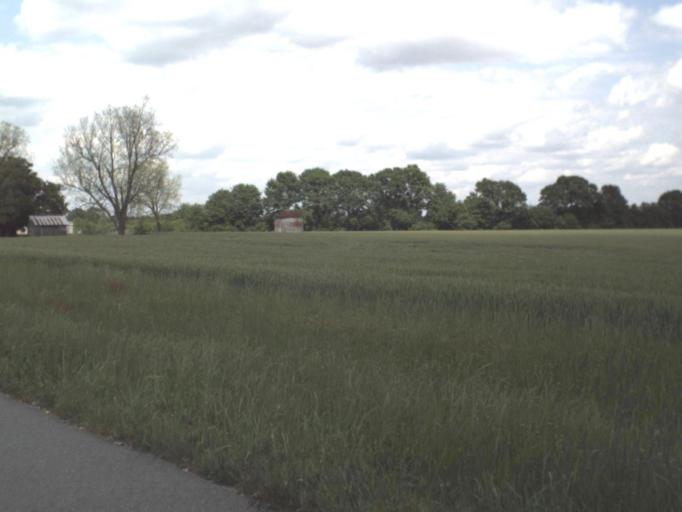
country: US
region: Alabama
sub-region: Escambia County
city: Atmore
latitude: 30.9757
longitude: -87.4894
